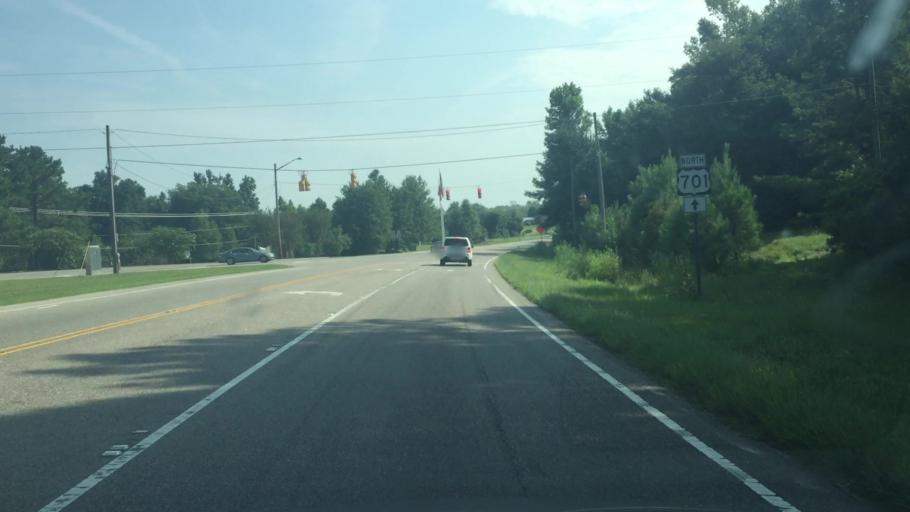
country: US
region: North Carolina
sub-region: Columbus County
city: Tabor City
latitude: 34.1559
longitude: -78.8585
